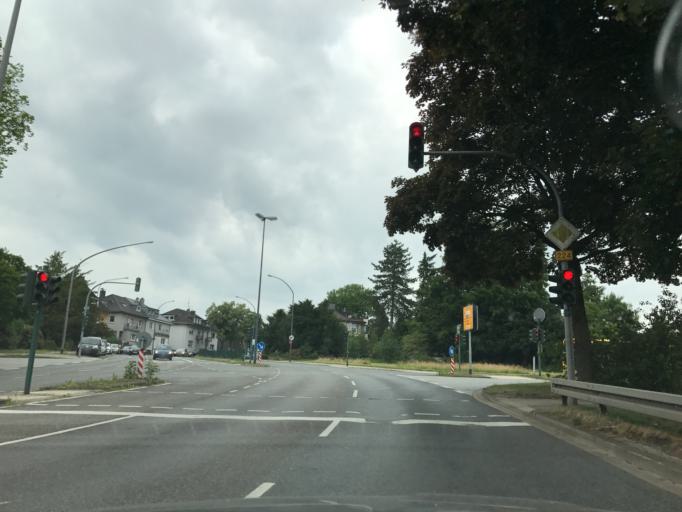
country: DE
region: North Rhine-Westphalia
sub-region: Regierungsbezirk Dusseldorf
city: Essen
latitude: 51.4085
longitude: 6.9936
